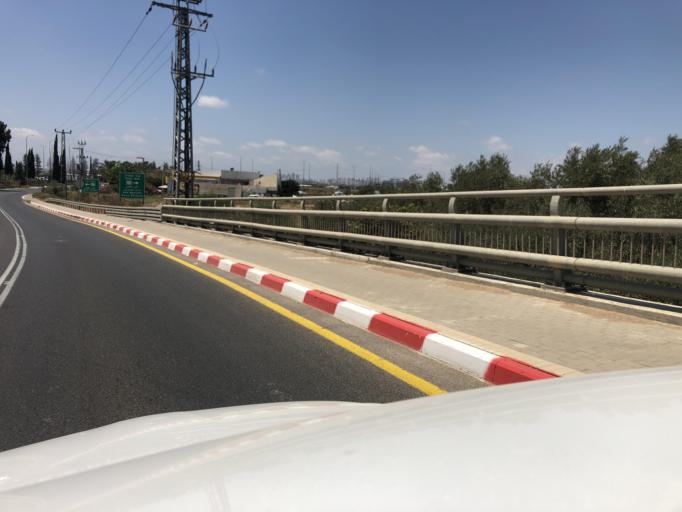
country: IL
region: Central District
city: Jaljulya
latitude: 32.1454
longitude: 34.9489
